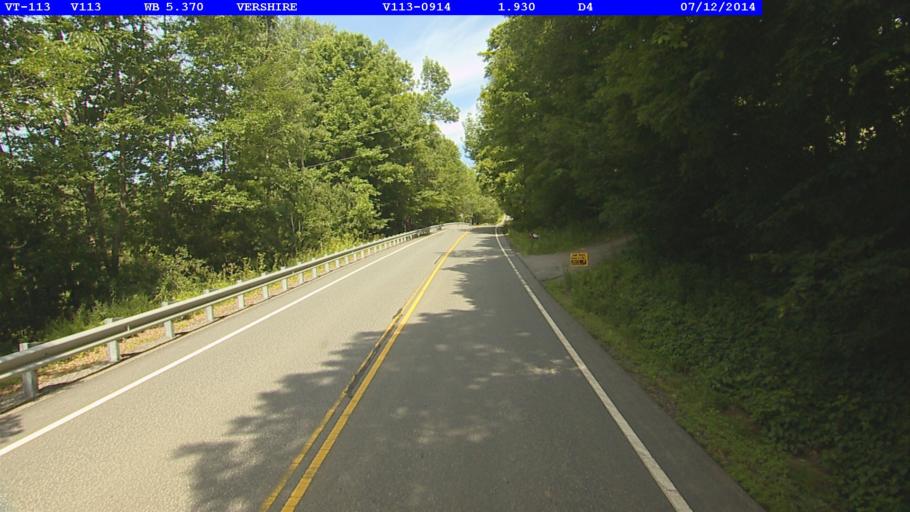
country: US
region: Vermont
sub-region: Orange County
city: Chelsea
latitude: 43.9771
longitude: -72.3528
